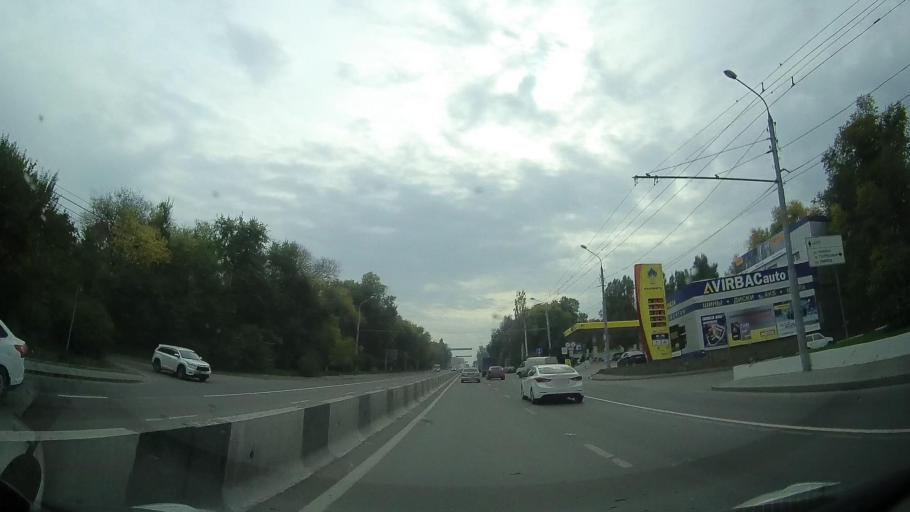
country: RU
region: Rostov
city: Rostov-na-Donu
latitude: 47.2432
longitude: 39.7131
